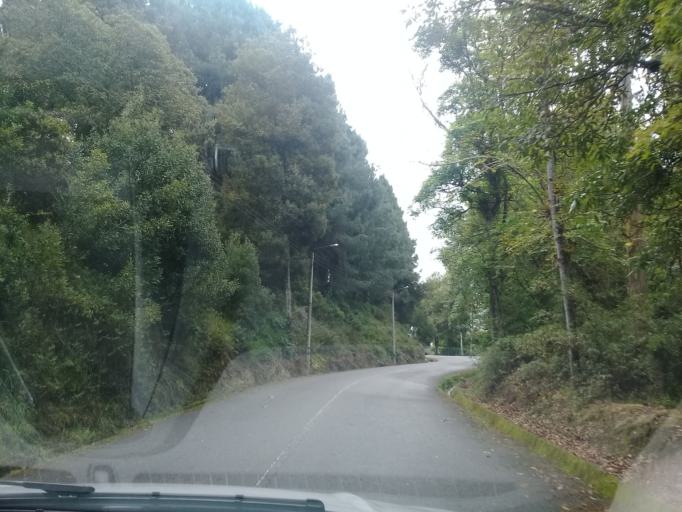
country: CO
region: Boyaca
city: Samaca
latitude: 5.4512
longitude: -73.4294
